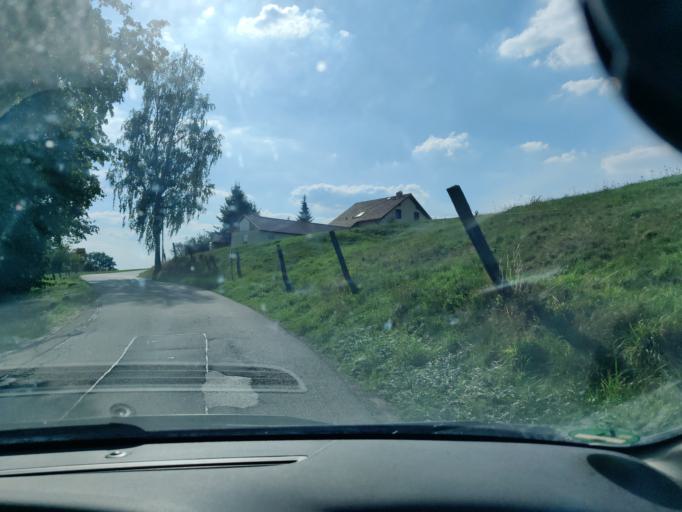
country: DE
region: Saxony
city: Mittweida
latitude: 51.0083
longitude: 13.0108
